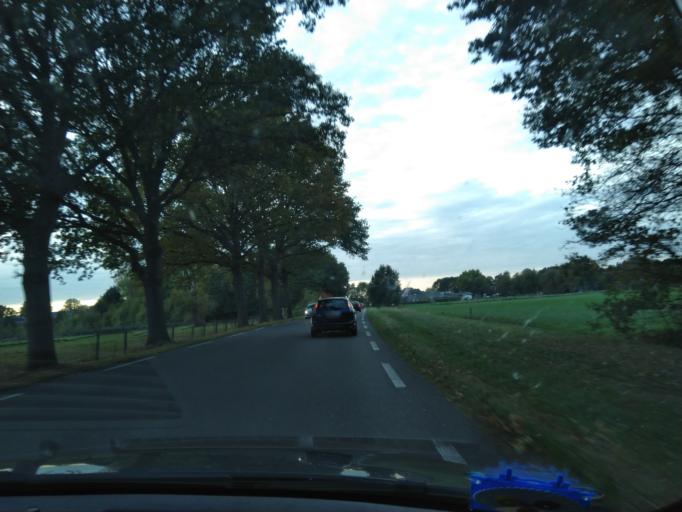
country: NL
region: Drenthe
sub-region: Gemeente Tynaarlo
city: Tynaarlo
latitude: 53.0794
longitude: 6.6167
